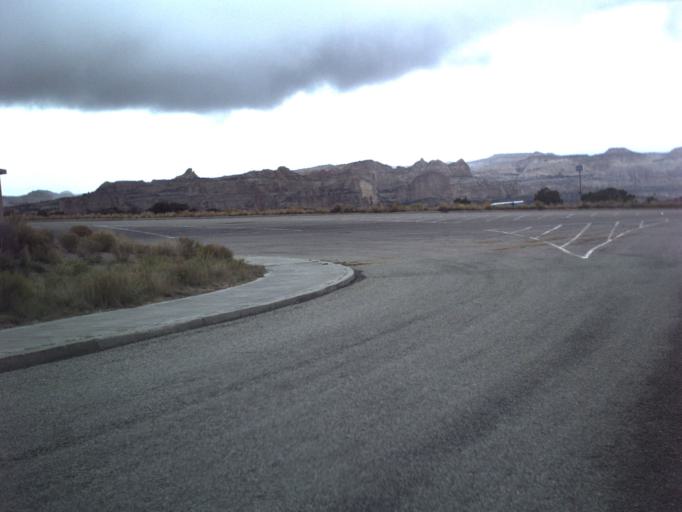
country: US
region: Utah
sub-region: Emery County
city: Ferron
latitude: 38.8621
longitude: -110.8117
